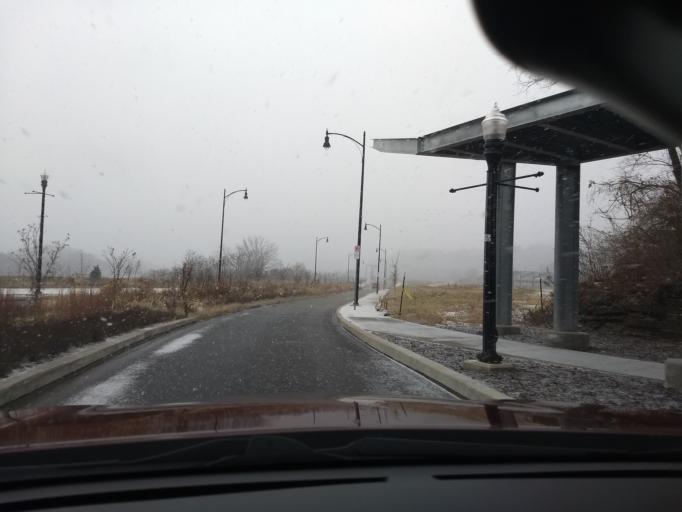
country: US
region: Pennsylvania
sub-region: Allegheny County
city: Mount Oliver
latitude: 40.4191
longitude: -79.9510
